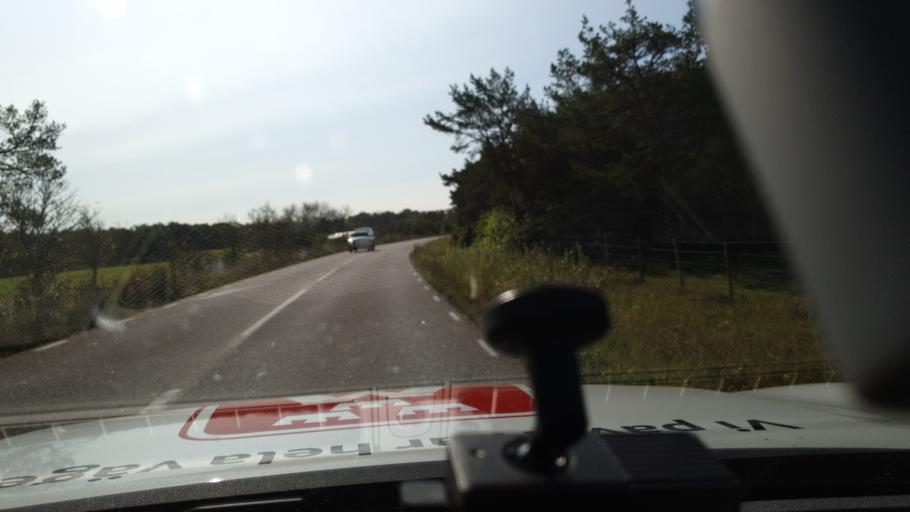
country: SE
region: Gotland
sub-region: Gotland
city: Hemse
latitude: 57.1012
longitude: 18.3029
